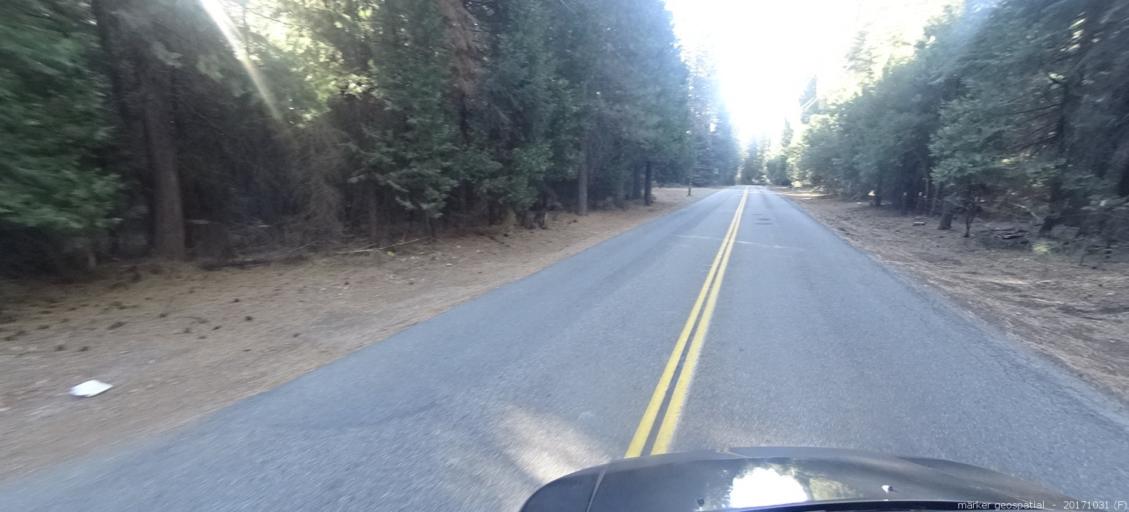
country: US
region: California
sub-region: Shasta County
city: Shingletown
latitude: 40.5278
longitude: -121.7469
